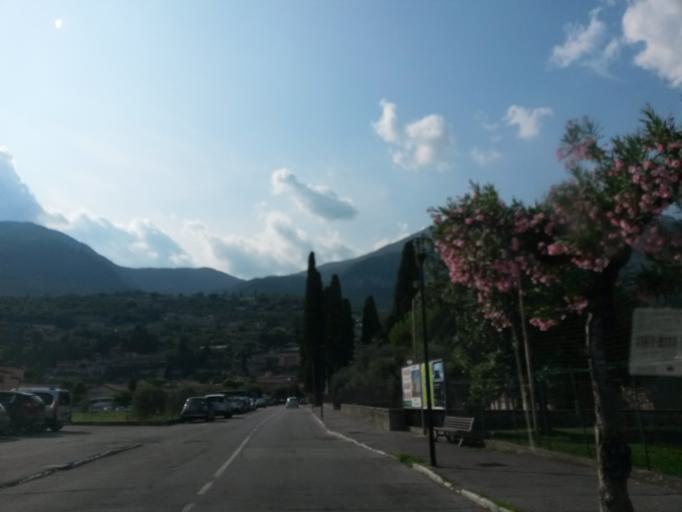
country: IT
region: Lombardy
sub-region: Provincia di Brescia
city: Toscolano Maderno
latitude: 45.6358
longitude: 10.6068
